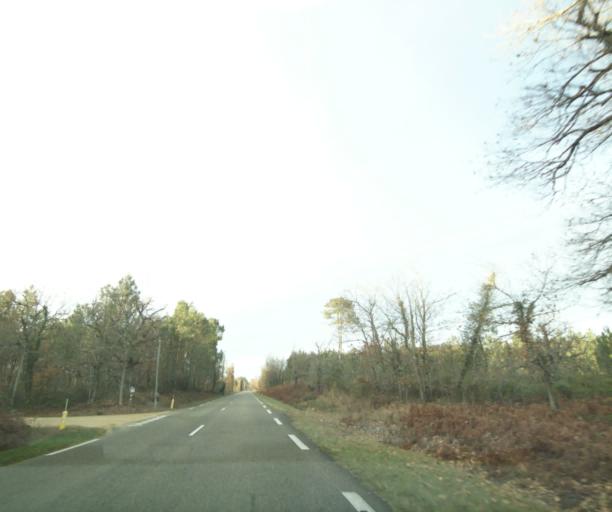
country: FR
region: Aquitaine
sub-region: Departement des Landes
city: Gabarret
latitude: 44.0497
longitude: -0.0417
